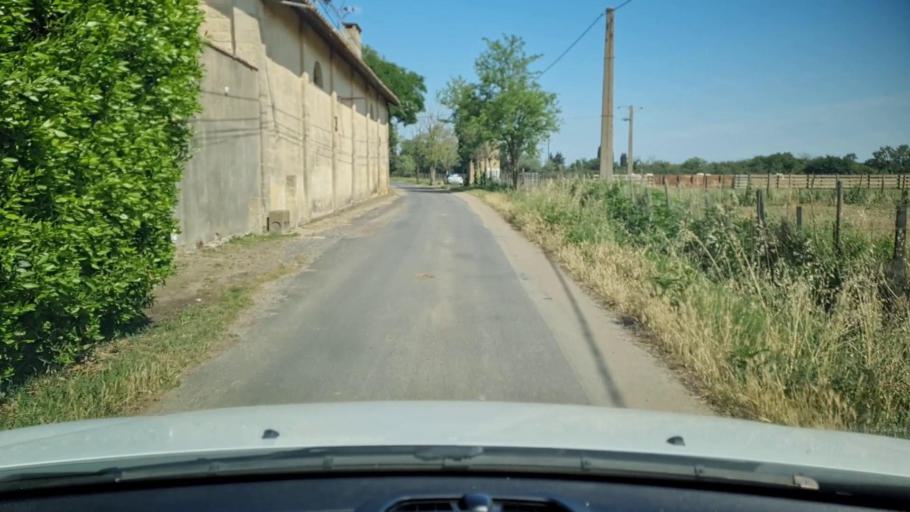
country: FR
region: Languedoc-Roussillon
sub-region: Departement du Gard
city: Le Cailar
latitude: 43.6506
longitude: 4.2402
